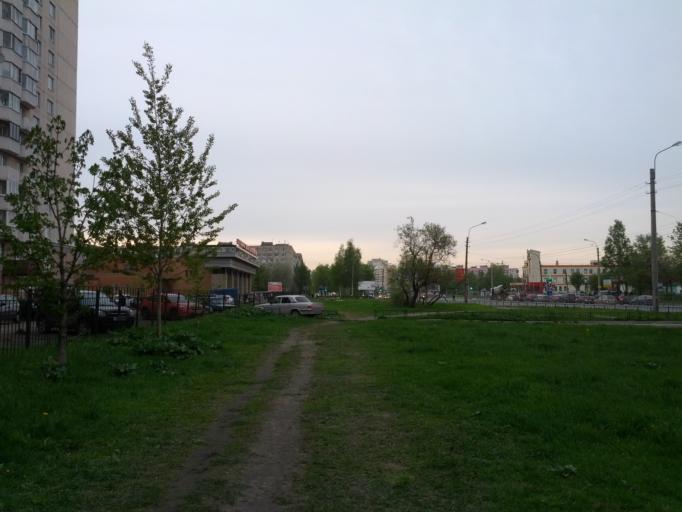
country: RU
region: Leningrad
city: Rybatskoye
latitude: 59.8907
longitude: 30.4897
